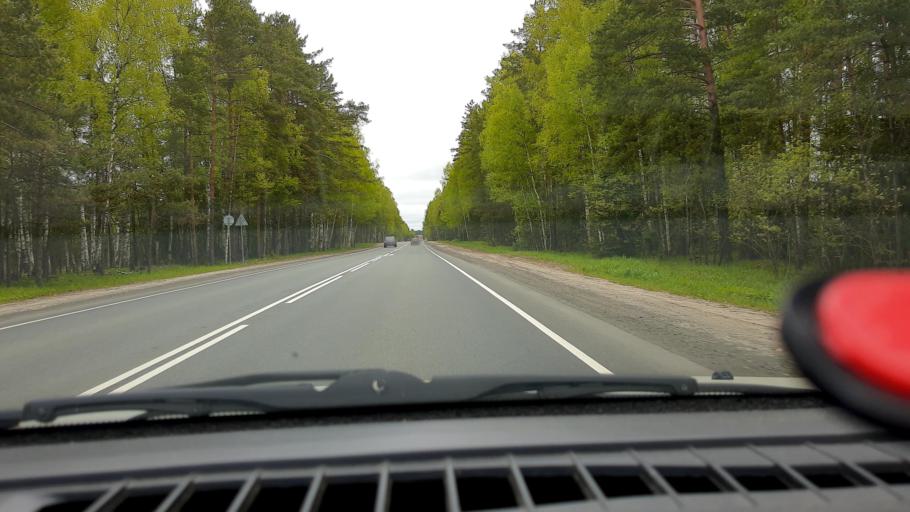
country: RU
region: Nizjnij Novgorod
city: Linda
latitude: 56.7212
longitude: 44.2785
